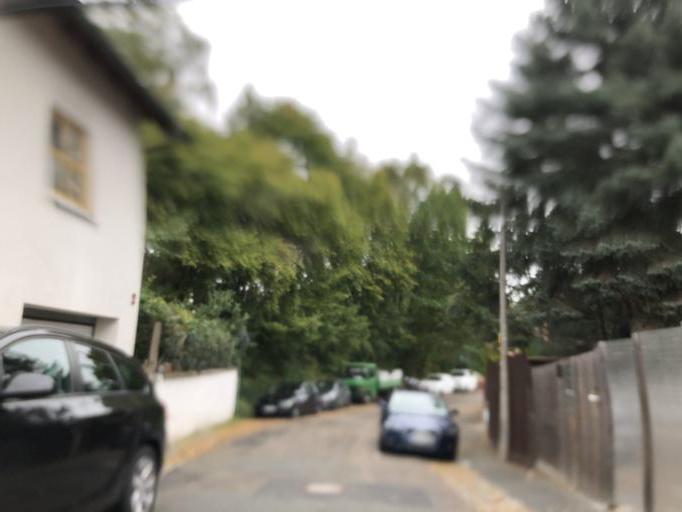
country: DE
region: Bavaria
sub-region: Regierungsbezirk Mittelfranken
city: Furth
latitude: 49.4616
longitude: 10.9703
